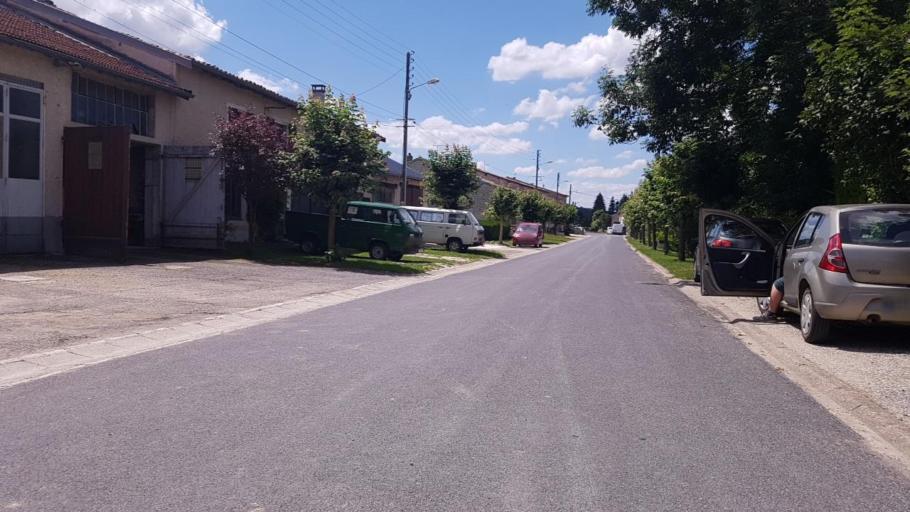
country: FR
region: Lorraine
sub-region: Departement de la Meuse
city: Vacon
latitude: 48.6448
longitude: 5.5140
